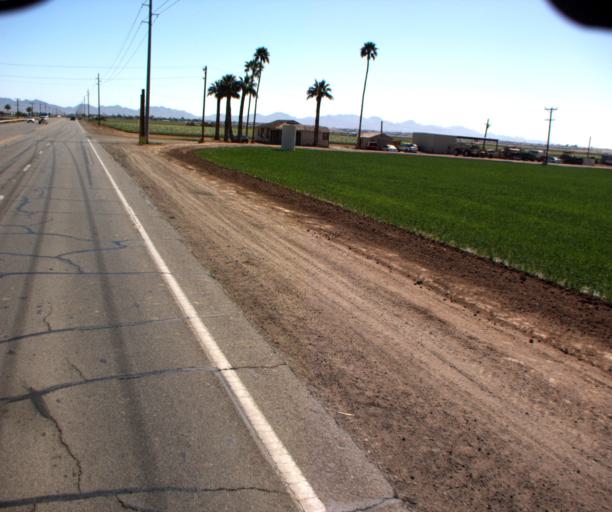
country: US
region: Arizona
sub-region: Yuma County
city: Yuma
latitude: 32.6988
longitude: -114.5654
